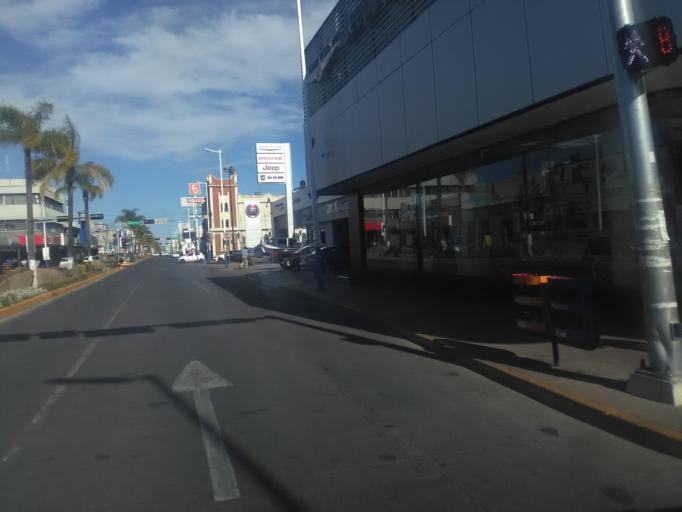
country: MX
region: Durango
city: Victoria de Durango
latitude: 24.0266
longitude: -104.6587
